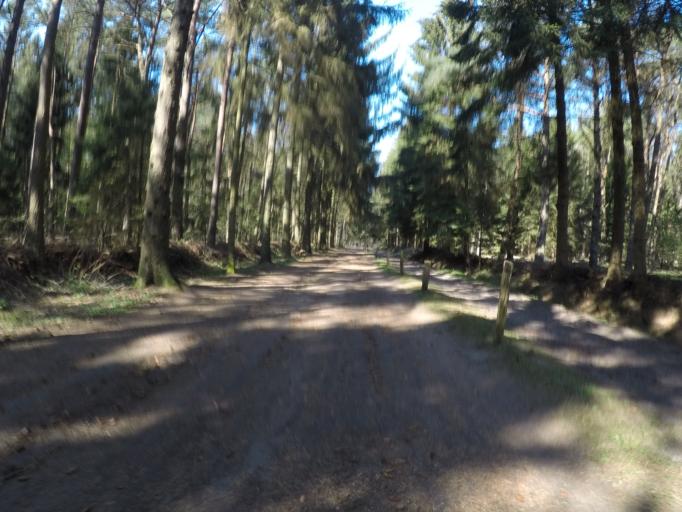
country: DE
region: Schleswig-Holstein
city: Appen
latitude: 53.6197
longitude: 9.7732
